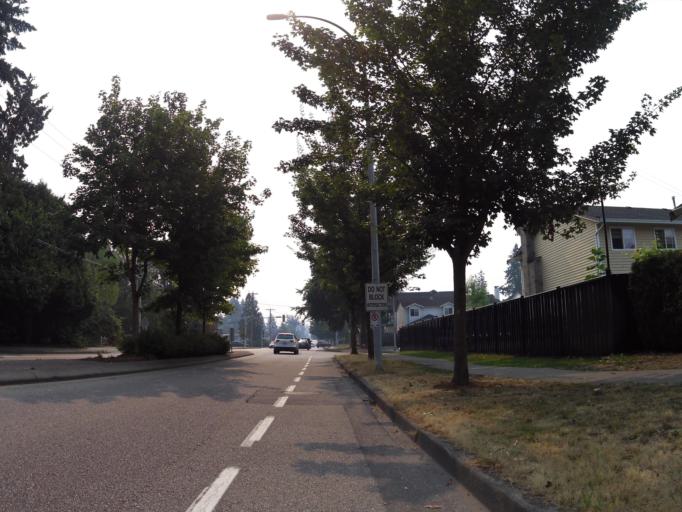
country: CA
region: British Columbia
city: Surrey
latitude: 49.1279
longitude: -122.8567
